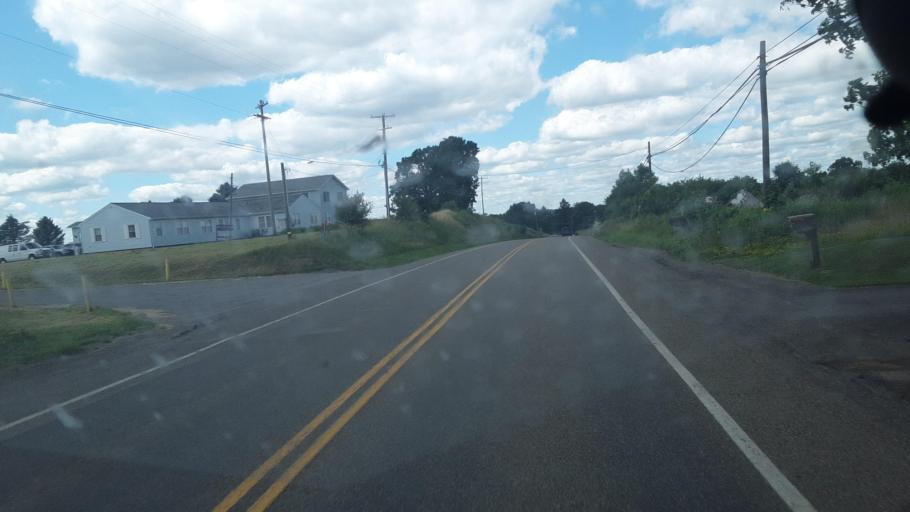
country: US
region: Pennsylvania
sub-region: Butler County
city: Prospect
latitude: 40.9450
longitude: -80.1530
